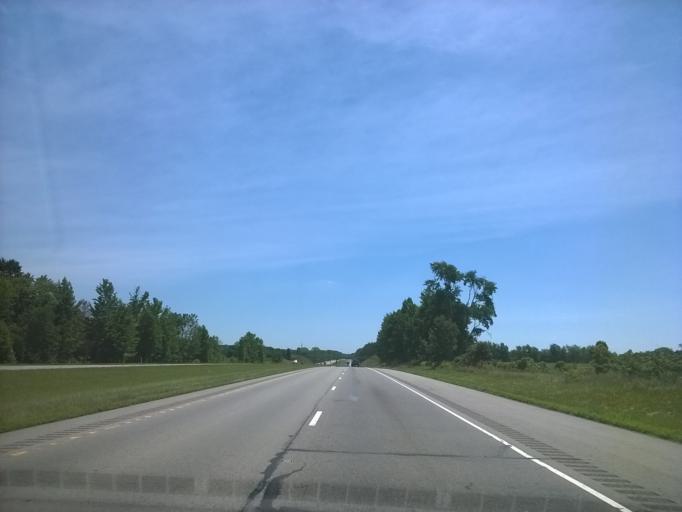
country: US
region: Indiana
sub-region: Ripley County
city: Sunman
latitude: 39.2854
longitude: -85.0456
